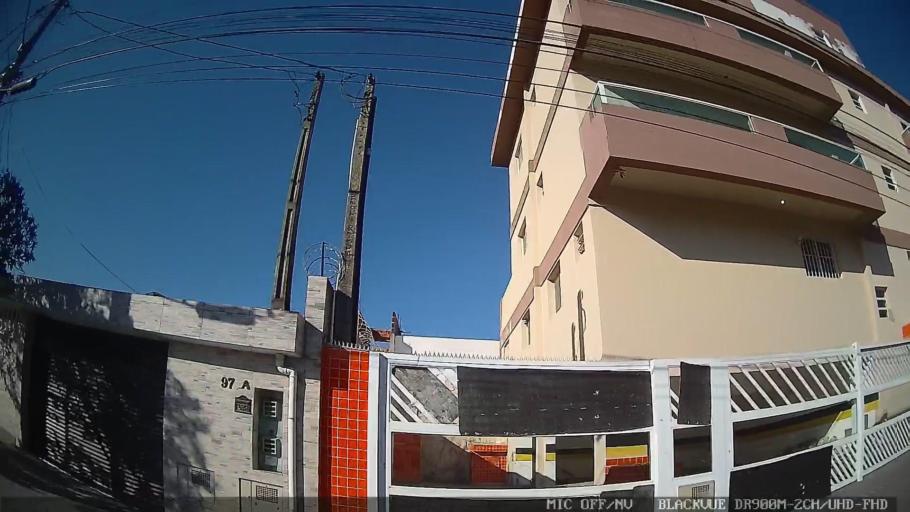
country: BR
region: Sao Paulo
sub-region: Guaruja
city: Guaruja
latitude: -23.9767
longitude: -46.2234
